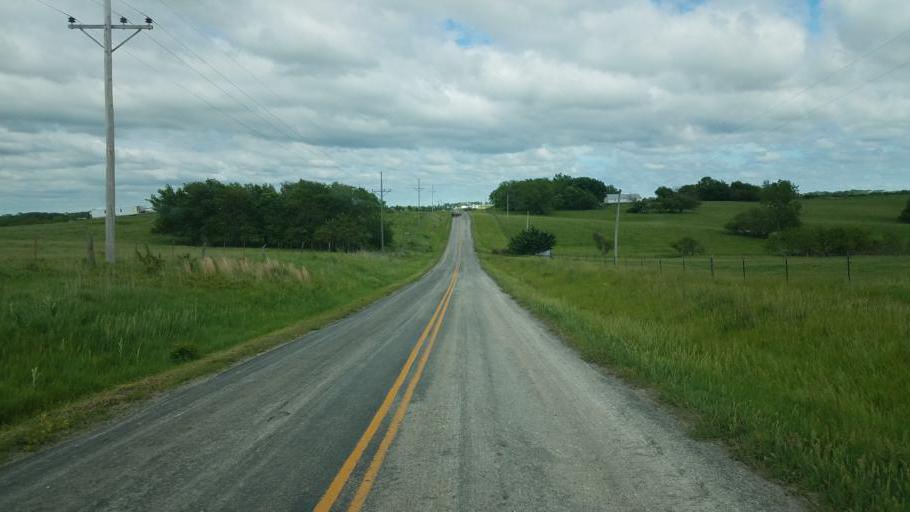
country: US
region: Missouri
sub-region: Mercer County
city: Princeton
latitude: 40.3002
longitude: -93.7222
